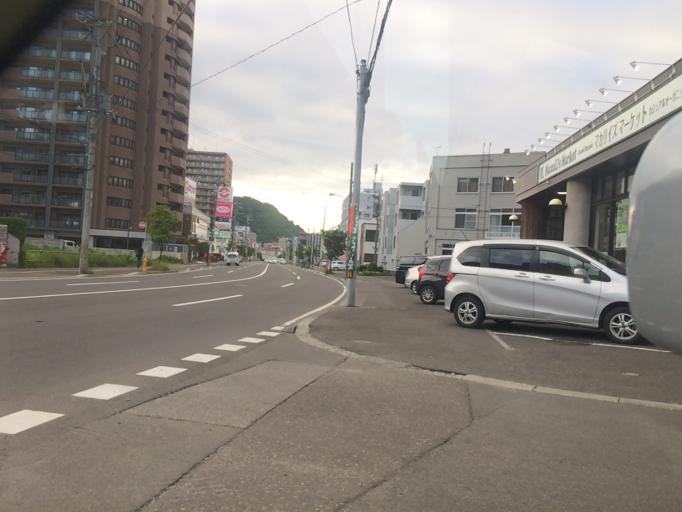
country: JP
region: Hokkaido
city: Sapporo
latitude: 43.0345
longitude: 141.3343
